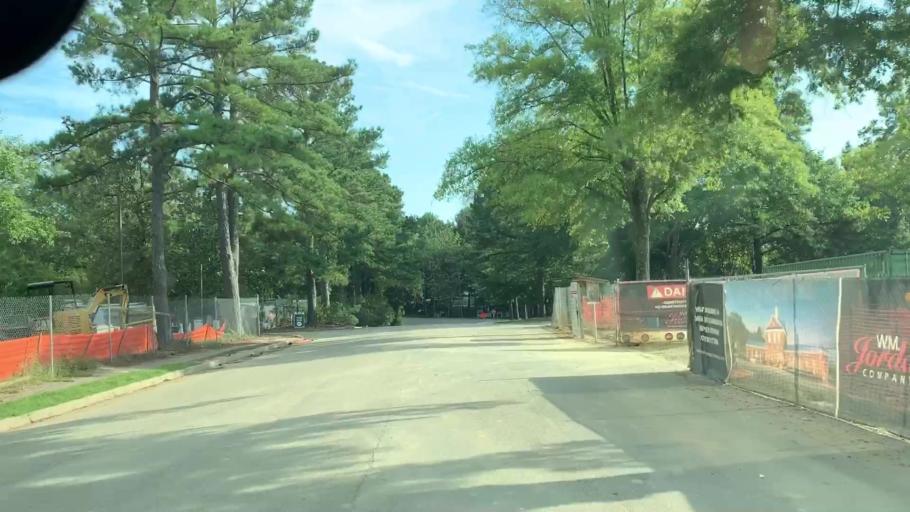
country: US
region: Virginia
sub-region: City of Williamsburg
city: Williamsburg
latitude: 37.2681
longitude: -76.7038
